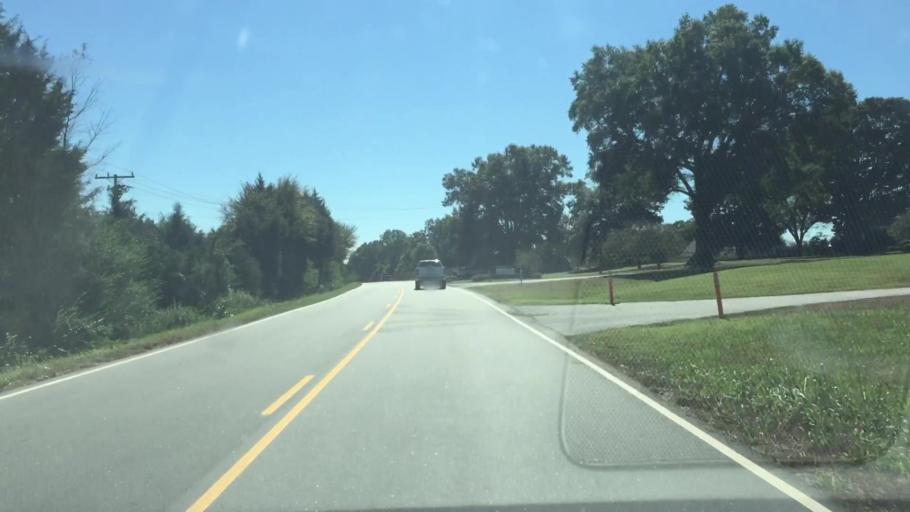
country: US
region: North Carolina
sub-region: Rowan County
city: Enochville
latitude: 35.4554
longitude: -80.7321
